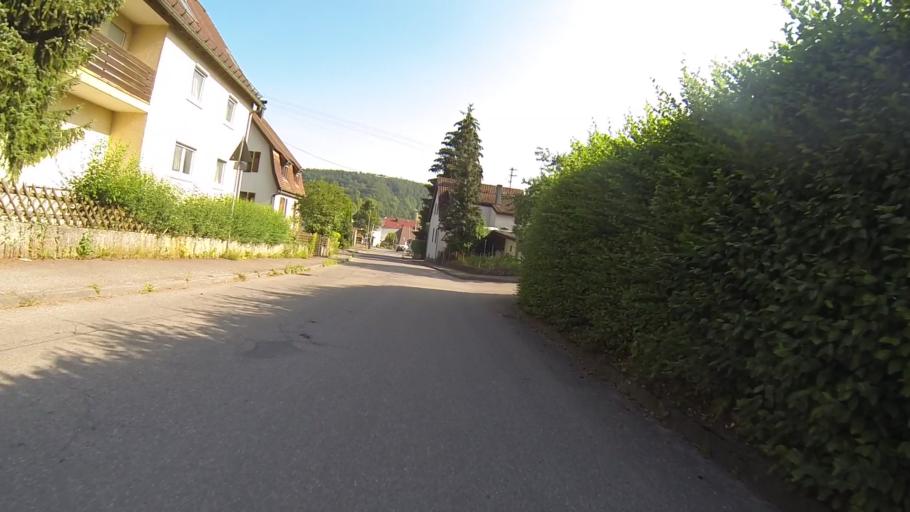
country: DE
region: Baden-Wuerttemberg
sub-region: Regierungsbezirk Stuttgart
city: Konigsbronn
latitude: 48.7297
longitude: 10.1355
